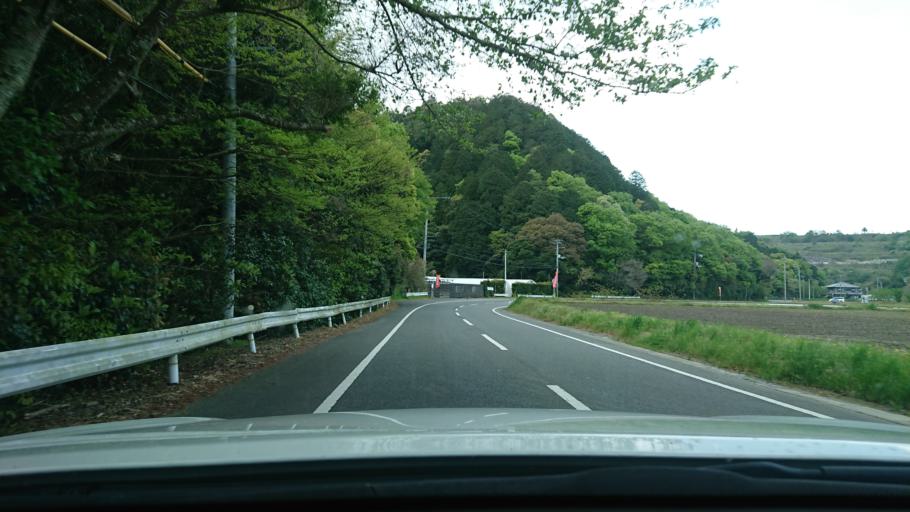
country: JP
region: Tokushima
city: Komatsushimacho
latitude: 33.9811
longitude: 134.5463
